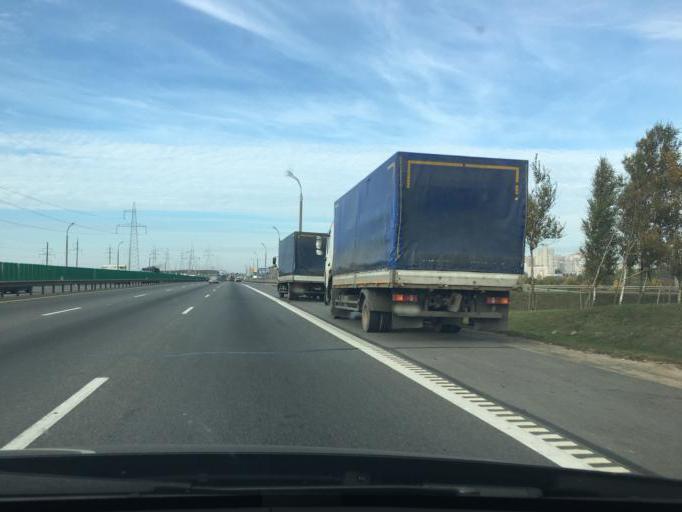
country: BY
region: Minsk
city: Malinovka
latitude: 53.8728
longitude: 27.4212
